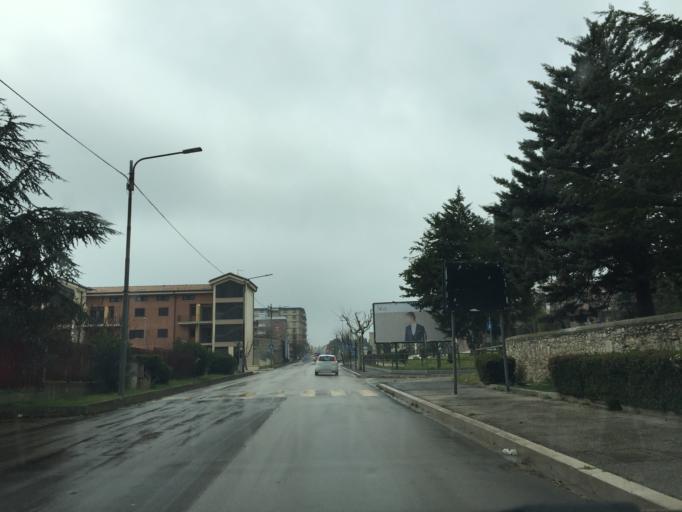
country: IT
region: Apulia
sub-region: Provincia di Foggia
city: Troia
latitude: 41.3668
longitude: 15.3251
